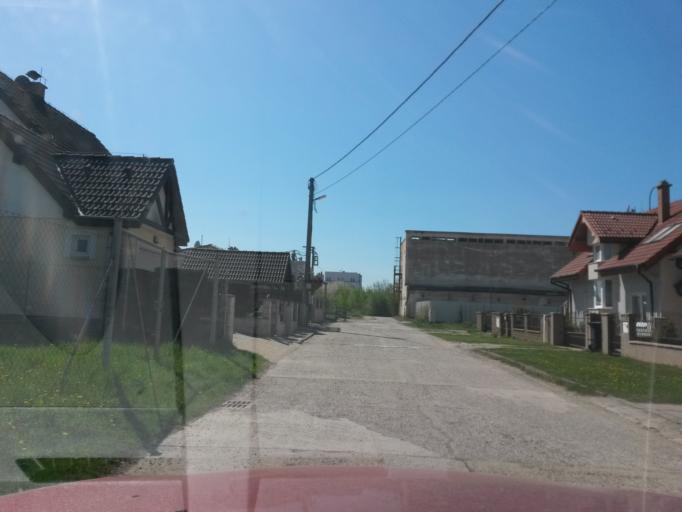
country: SK
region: Kosicky
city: Kosice
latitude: 48.6807
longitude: 21.2733
